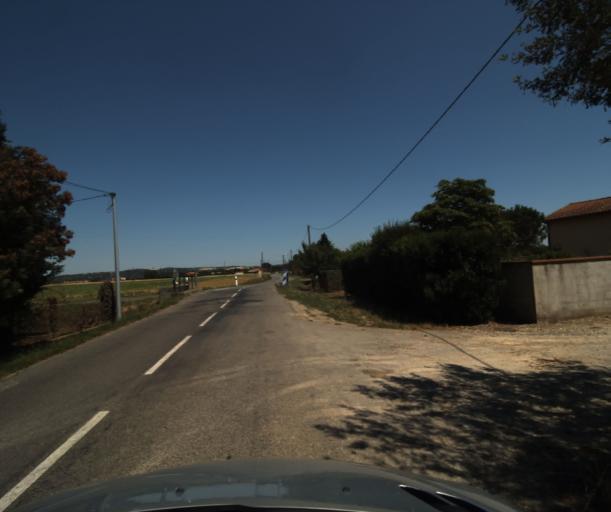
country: FR
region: Midi-Pyrenees
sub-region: Departement de la Haute-Garonne
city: Saubens
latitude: 43.4774
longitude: 1.3624
